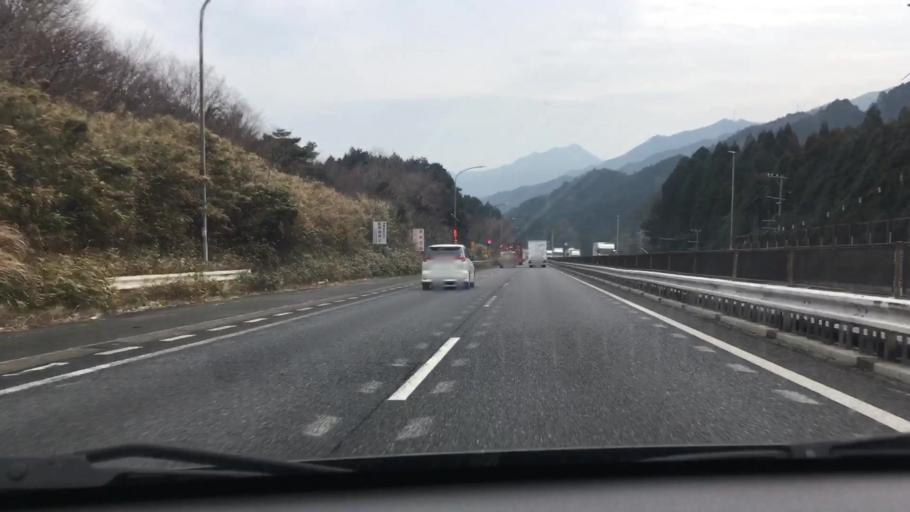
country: JP
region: Mie
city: Kameyama
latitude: 34.8351
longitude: 136.2905
